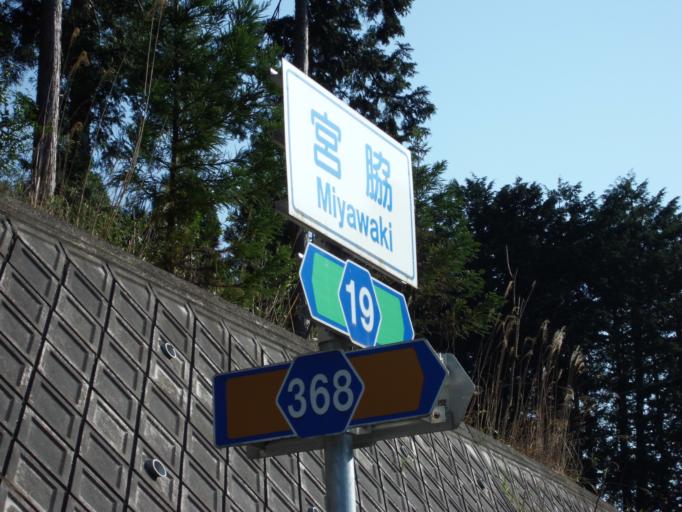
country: JP
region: Kyoto
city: Kameoka
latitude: 35.2561
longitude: 135.5655
